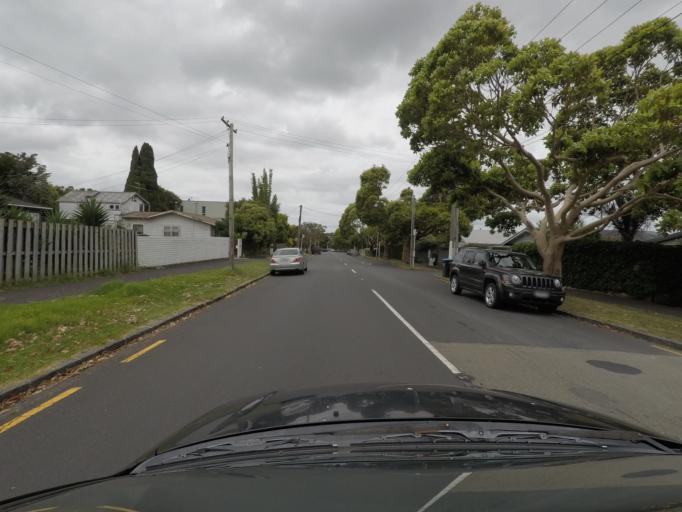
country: NZ
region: Auckland
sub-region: Auckland
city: Rosebank
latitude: -36.8624
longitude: 174.7082
